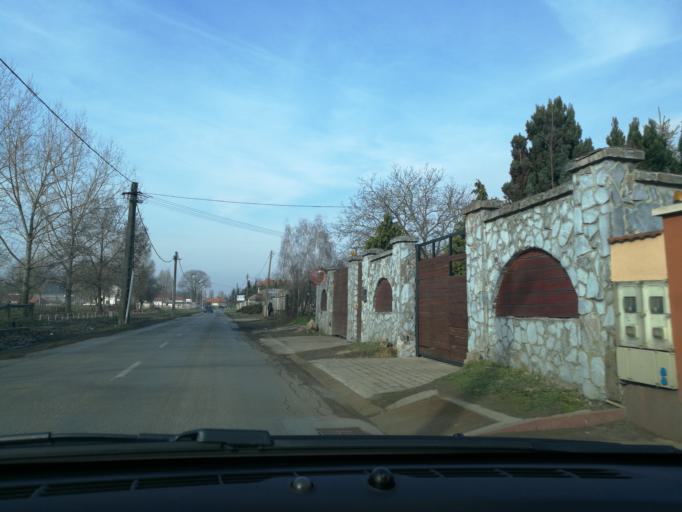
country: HU
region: Szabolcs-Szatmar-Bereg
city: Nyiregyhaza
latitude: 47.9630
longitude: 21.7349
